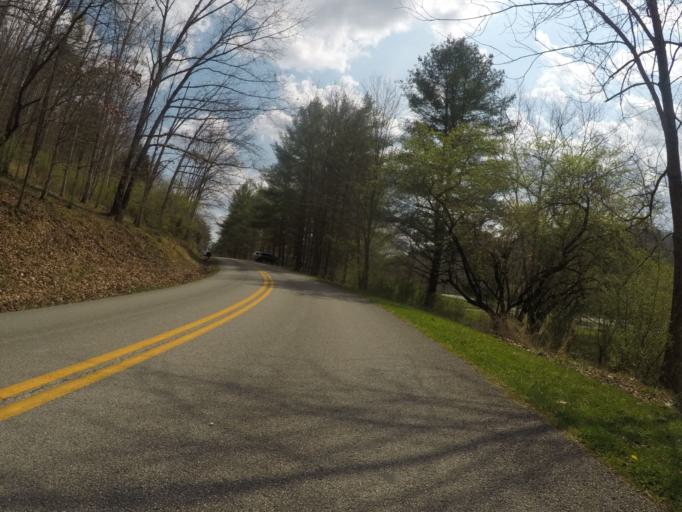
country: US
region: West Virginia
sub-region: Wayne County
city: Lavalette
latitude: 38.3088
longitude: -82.3581
